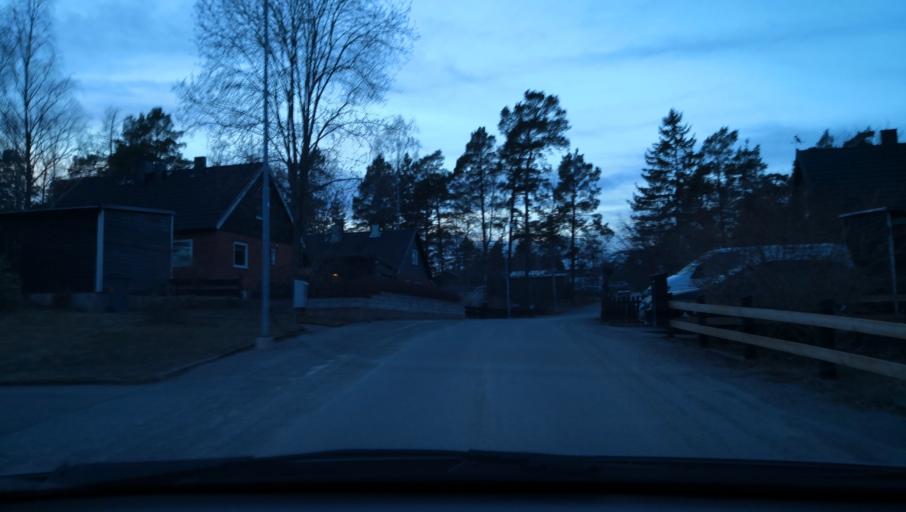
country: SE
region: Stockholm
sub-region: Varmdo Kommun
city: Gustavsberg
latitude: 59.3352
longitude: 18.3911
